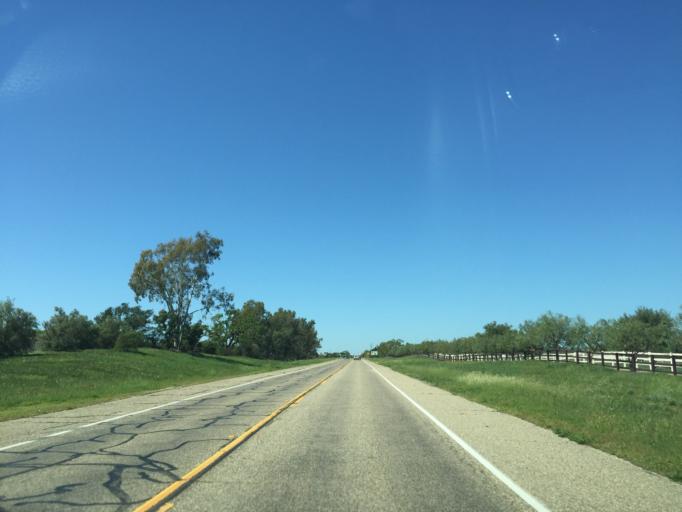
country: US
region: California
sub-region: Santa Barbara County
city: Santa Ynez
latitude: 34.6297
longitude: -120.0776
